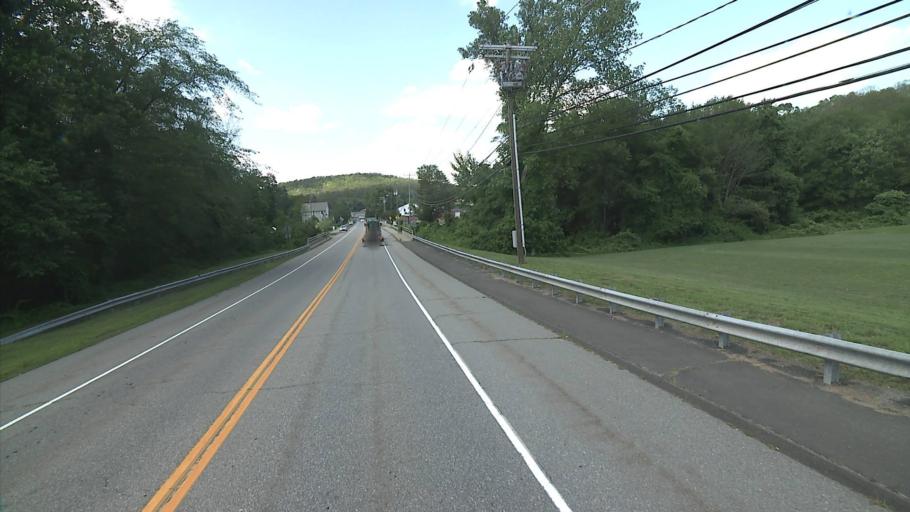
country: US
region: Connecticut
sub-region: Middlesex County
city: Higganum
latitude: 41.4937
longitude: -72.5582
